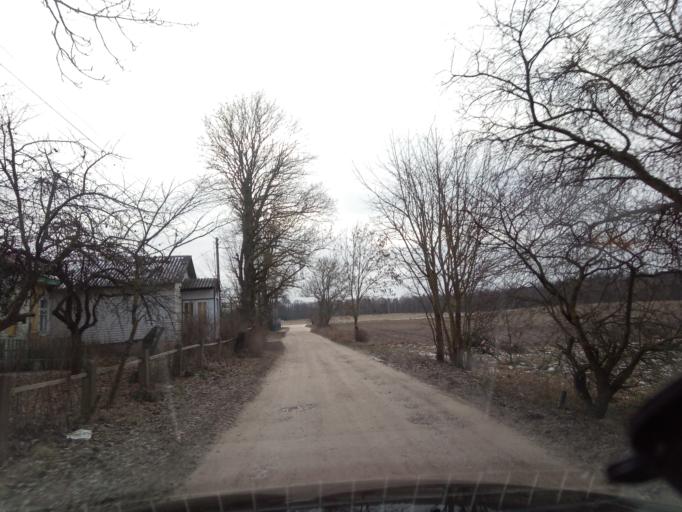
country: LT
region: Alytaus apskritis
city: Varena
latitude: 54.1243
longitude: 24.6468
